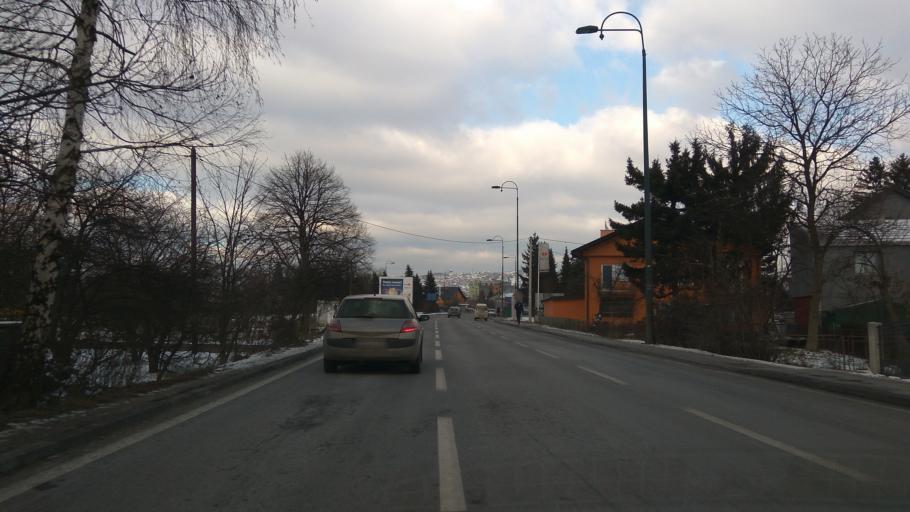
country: BA
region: Federation of Bosnia and Herzegovina
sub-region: Kanton Sarajevo
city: Sarajevo
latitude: 43.8357
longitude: 18.3160
